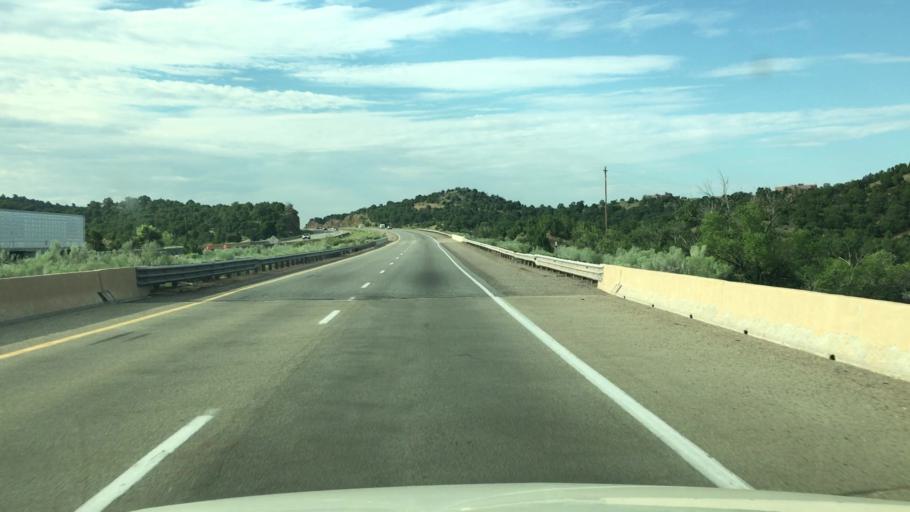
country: US
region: New Mexico
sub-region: Santa Fe County
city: Santa Fe
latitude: 35.6213
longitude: -105.9198
